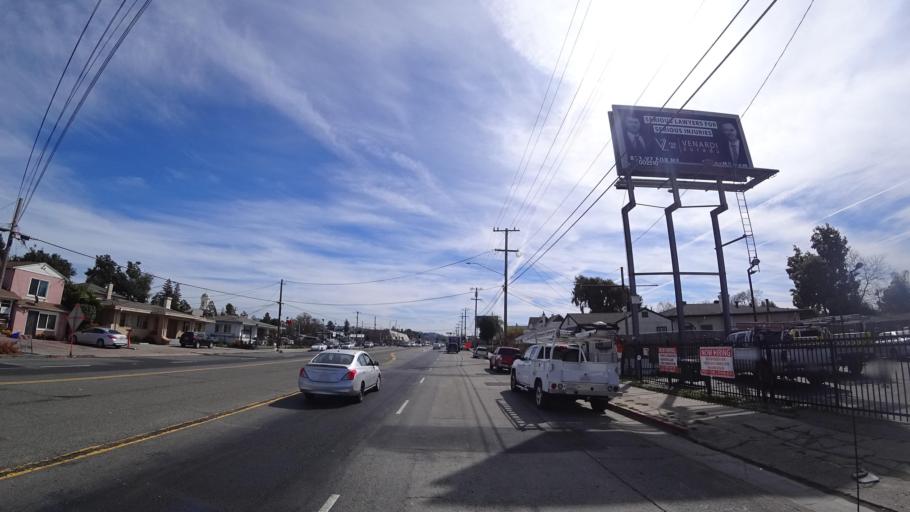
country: US
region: California
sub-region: Alameda County
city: Cherryland
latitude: 37.6812
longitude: -122.0953
